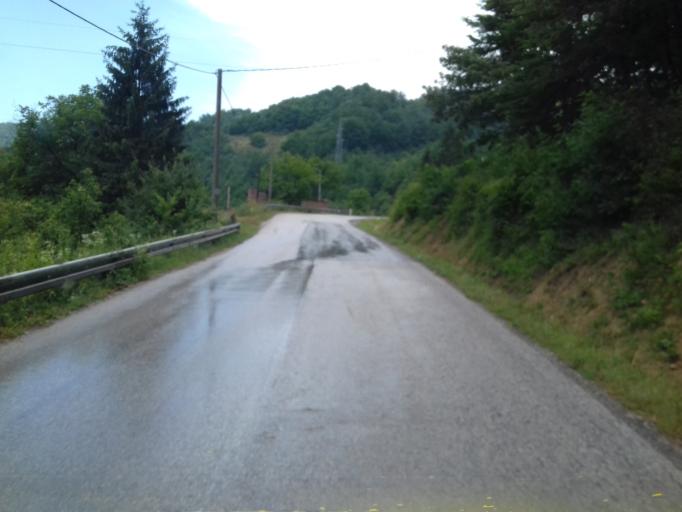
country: BA
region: Federation of Bosnia and Herzegovina
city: Kiseljak
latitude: 43.9546
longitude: 18.1256
